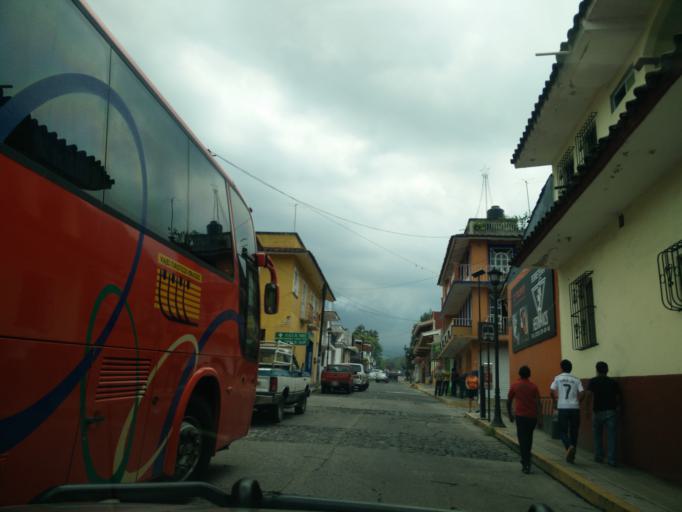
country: MX
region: Veracruz
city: Xico
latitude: 19.4229
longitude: -97.0095
